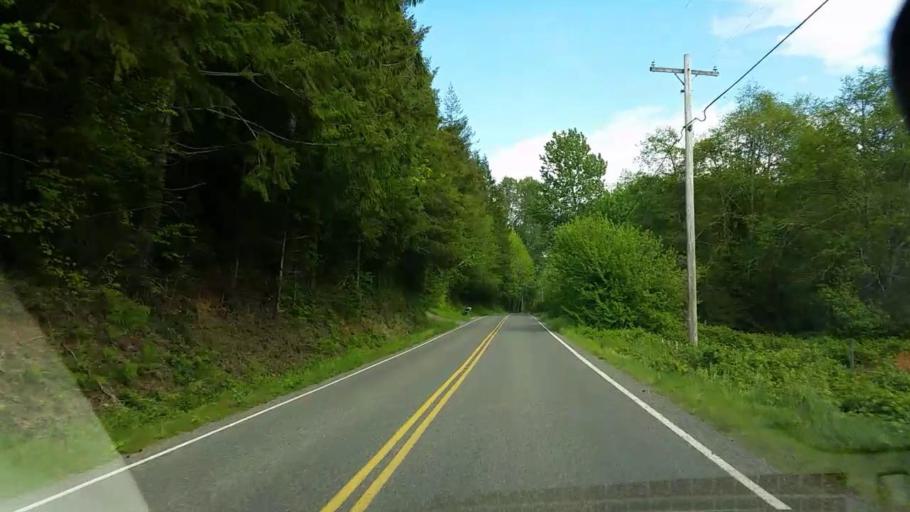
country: US
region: Washington
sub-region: Mason County
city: Shelton
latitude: 47.3202
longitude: -123.2678
